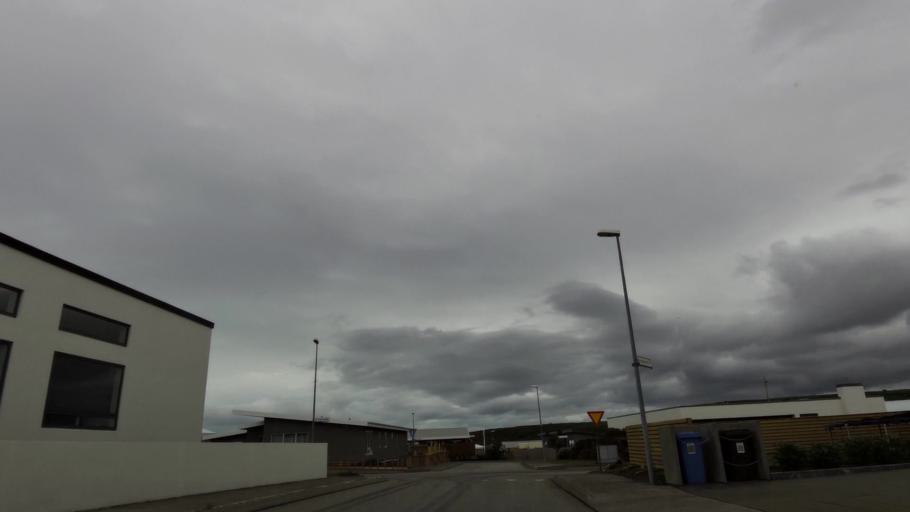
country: IS
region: Capital Region
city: Hafnarfjoerdur
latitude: 64.0430
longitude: -21.9668
